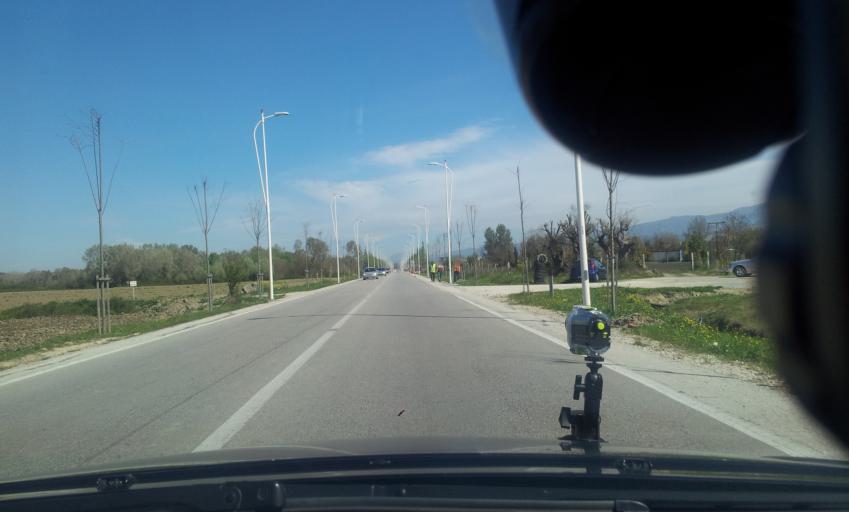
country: AL
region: Tirane
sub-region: Rrethi i Tiranes
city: Berxull
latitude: 41.3898
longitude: 19.7041
